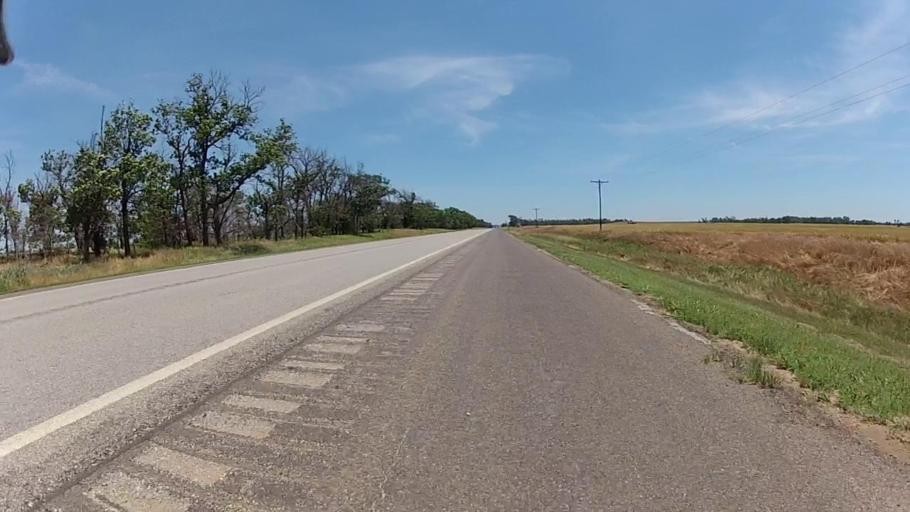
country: US
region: Kansas
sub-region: Barber County
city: Medicine Lodge
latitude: 37.2536
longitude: -98.3846
